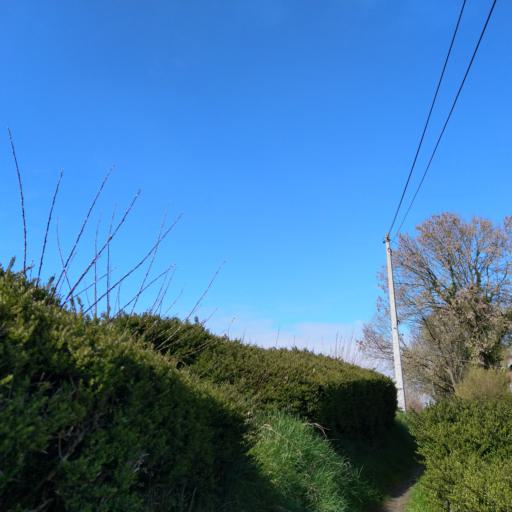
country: BE
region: Wallonia
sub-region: Province du Hainaut
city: Brugelette
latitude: 50.5898
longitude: 3.8736
